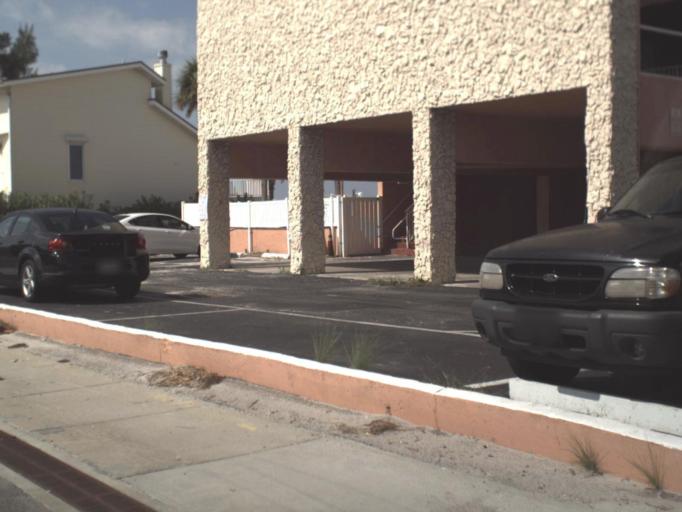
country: US
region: Florida
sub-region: Pinellas County
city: Treasure Island
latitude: 27.7586
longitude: -82.7655
